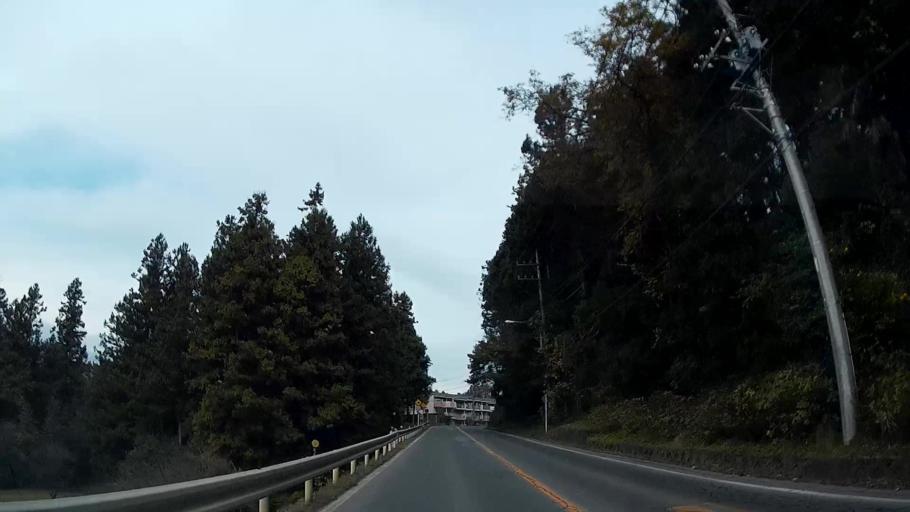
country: JP
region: Saitama
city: Chichibu
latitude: 35.9661
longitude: 139.0599
